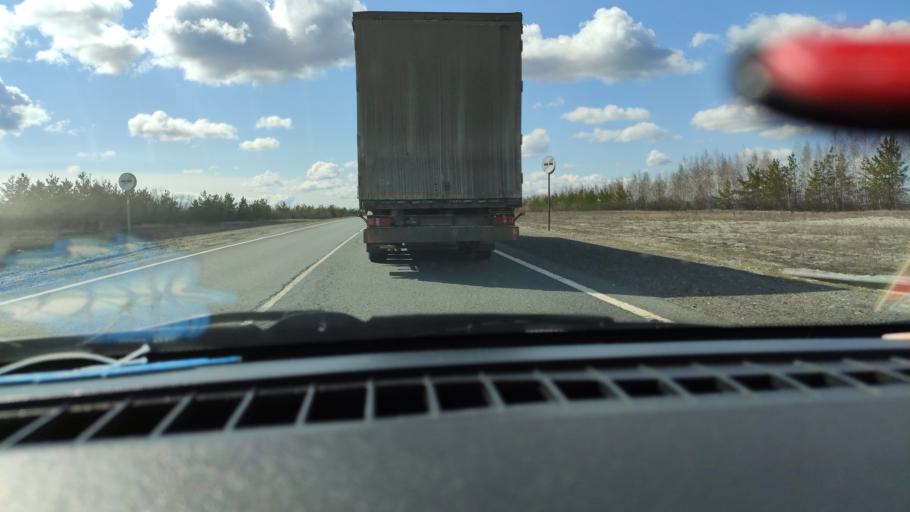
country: RU
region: Samara
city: Syzran'
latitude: 52.8809
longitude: 48.2921
